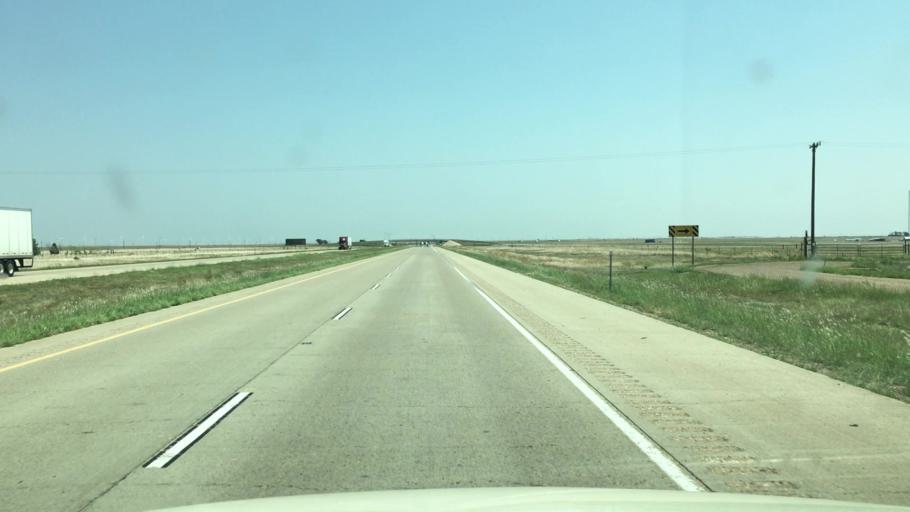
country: US
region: Texas
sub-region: Oldham County
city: Vega
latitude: 35.2367
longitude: -102.4177
